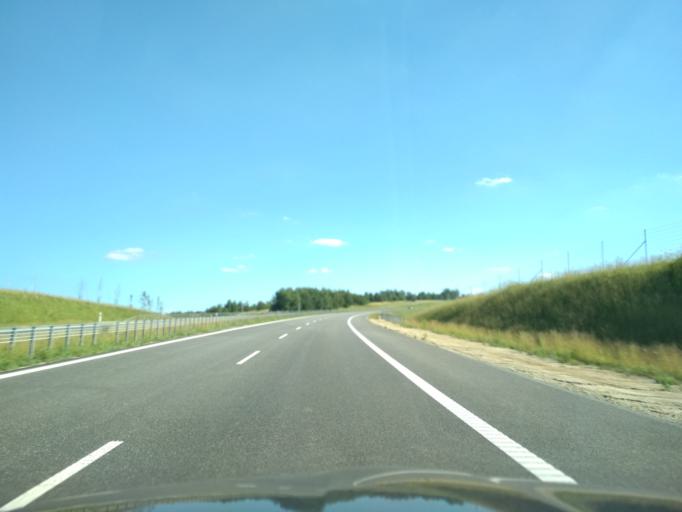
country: PL
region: Subcarpathian Voivodeship
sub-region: Rzeszow
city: Przybyszowka
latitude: 50.0440
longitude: 21.9328
